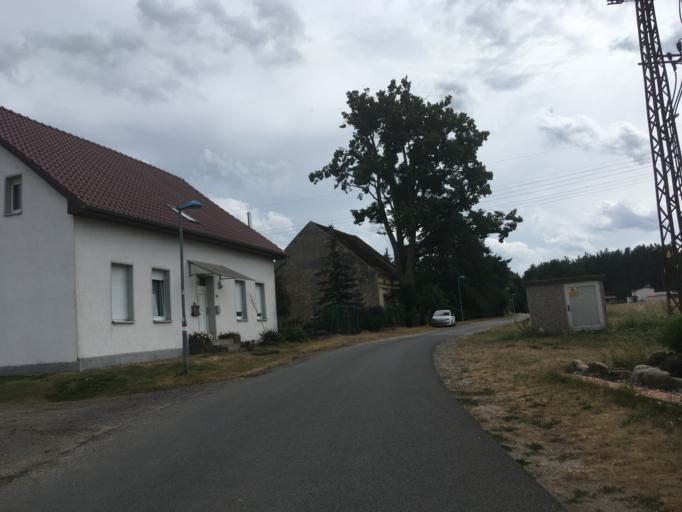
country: DE
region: Brandenburg
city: Chorin
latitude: 52.9312
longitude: 13.8612
